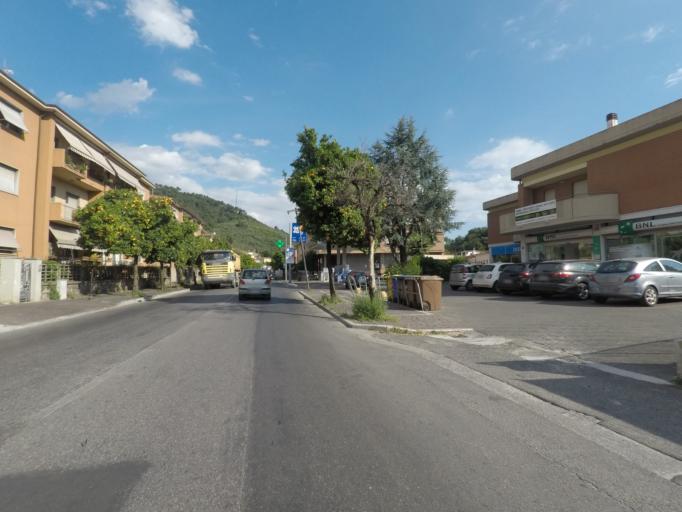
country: IT
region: Tuscany
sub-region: Provincia di Massa-Carrara
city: Massa
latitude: 44.0337
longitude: 10.1414
